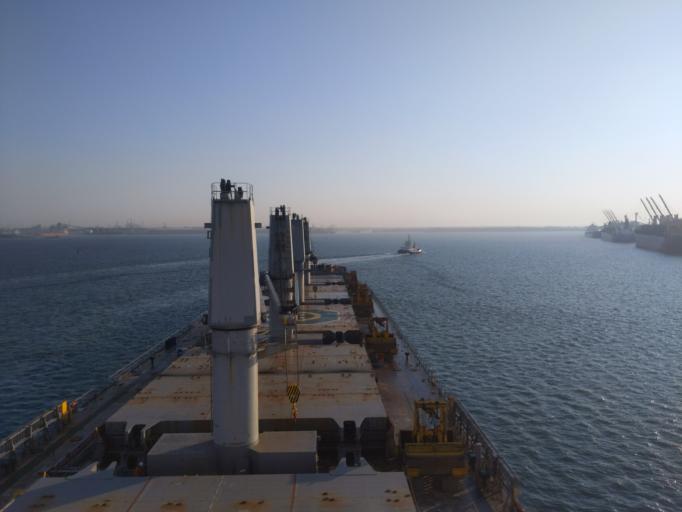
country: ZA
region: KwaZulu-Natal
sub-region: uThungulu District Municipality
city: Richards Bay
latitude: -28.8196
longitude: 32.0460
